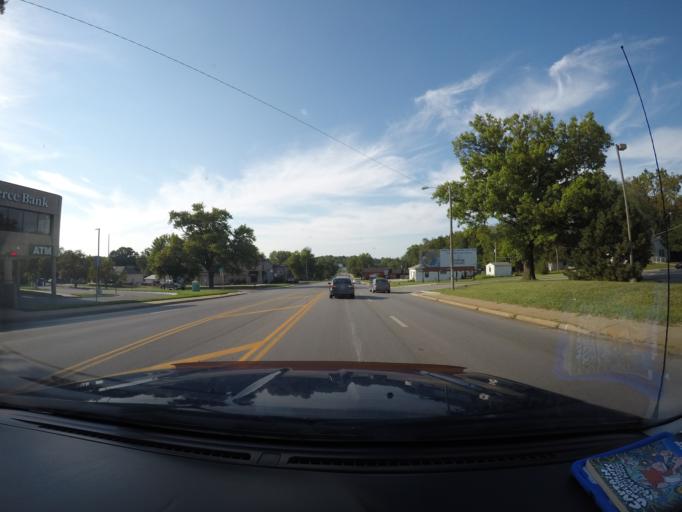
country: US
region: Kansas
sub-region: Leavenworth County
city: Leavenworth
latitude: 39.2892
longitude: -94.9069
